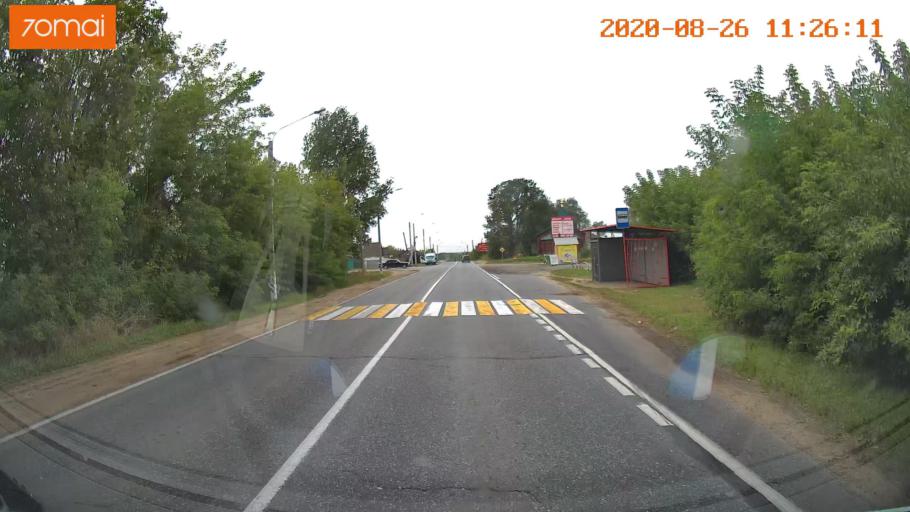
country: RU
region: Rjazan
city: Shilovo
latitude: 54.3356
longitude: 40.9529
